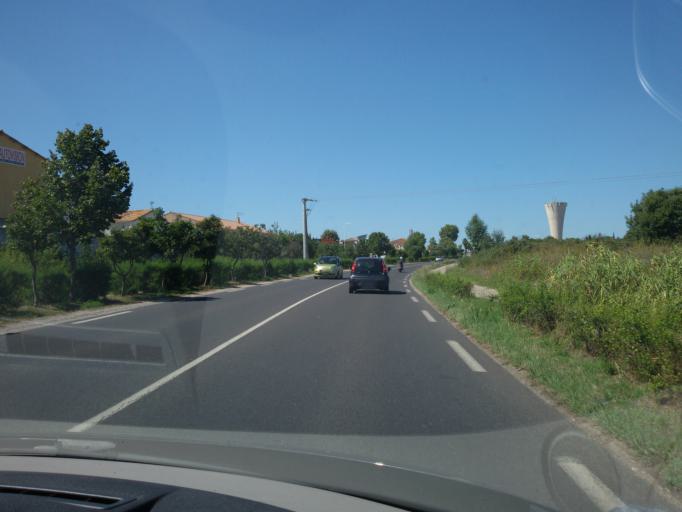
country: FR
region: Languedoc-Roussillon
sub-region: Departement de l'Herault
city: Villeneuve-les-Maguelone
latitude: 43.5376
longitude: 3.8605
